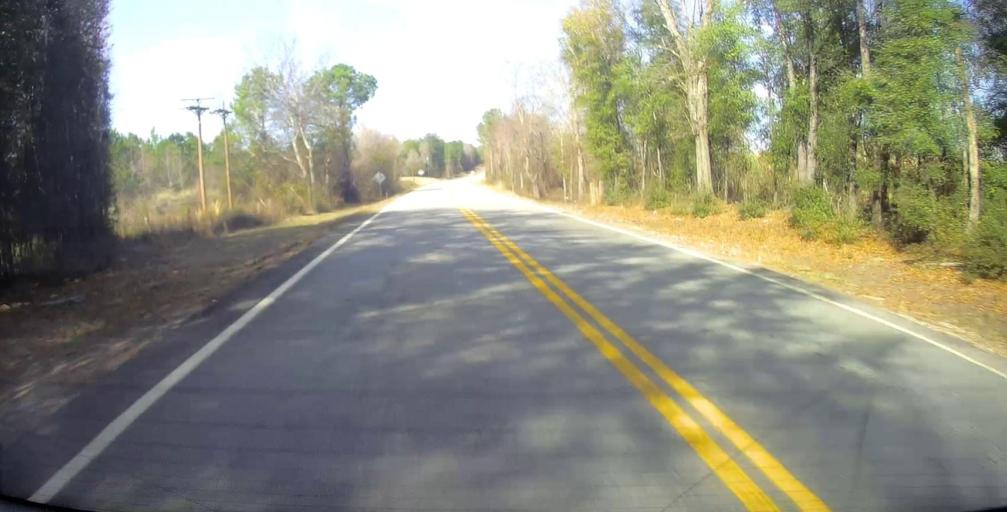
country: US
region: Georgia
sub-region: Twiggs County
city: Jeffersonville
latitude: 32.7761
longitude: -83.3329
